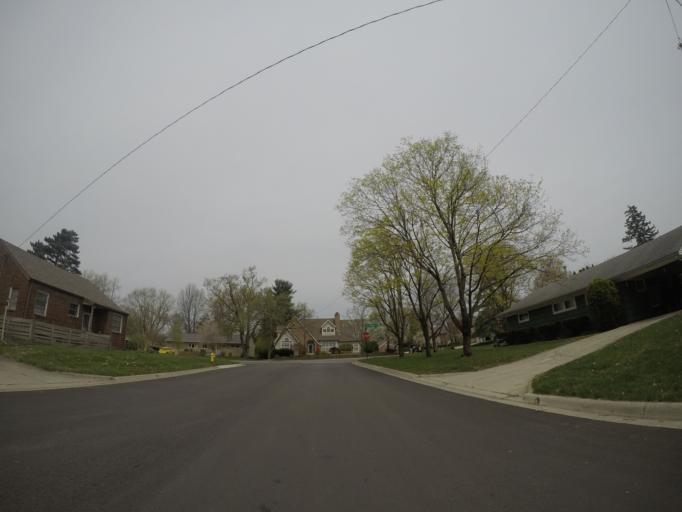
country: US
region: Ohio
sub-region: Franklin County
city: Upper Arlington
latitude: 40.0192
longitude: -83.0757
